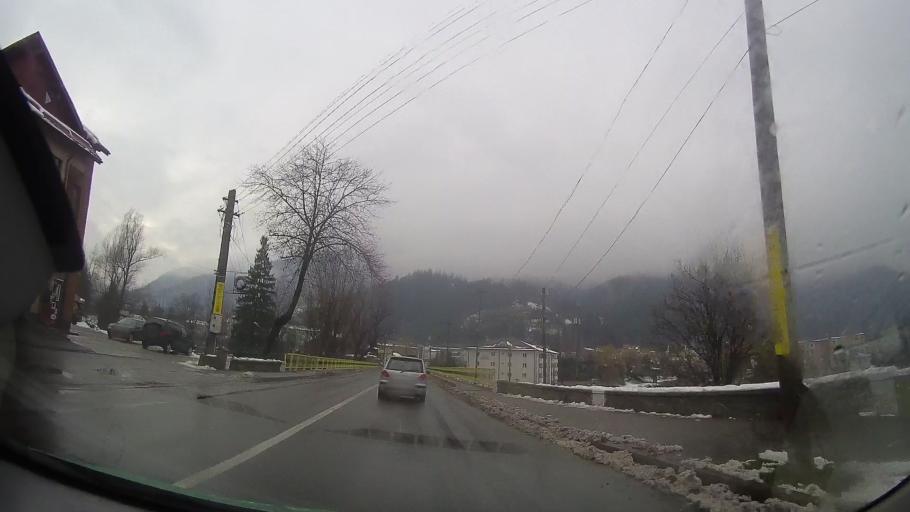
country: RO
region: Neamt
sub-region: Comuna Bicaz
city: Dodeni
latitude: 46.9107
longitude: 26.0922
